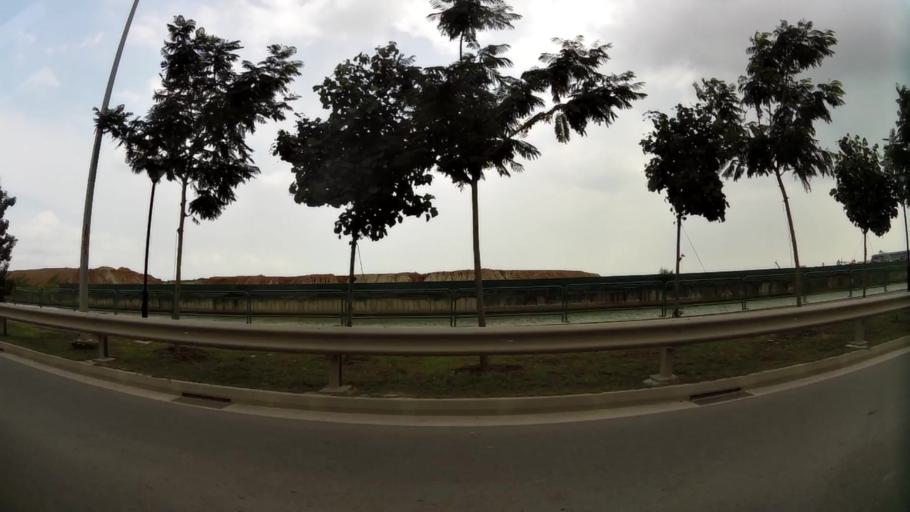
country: SG
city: Singapore
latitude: 1.3303
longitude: 103.9893
